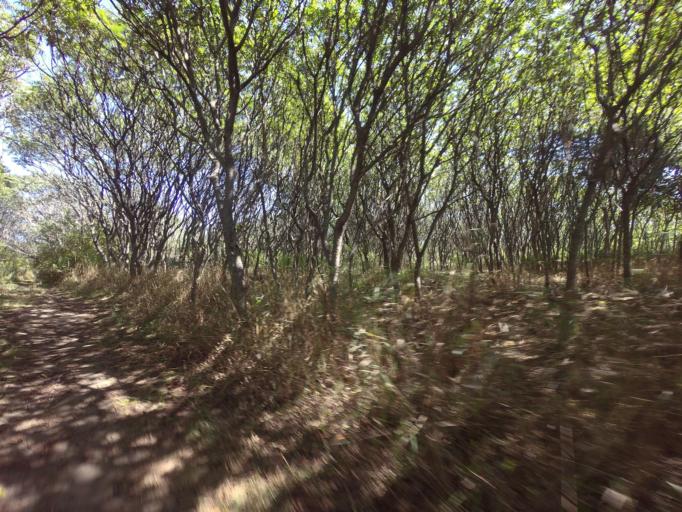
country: CA
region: Ontario
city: Orangeville
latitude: 43.8208
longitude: -80.0183
